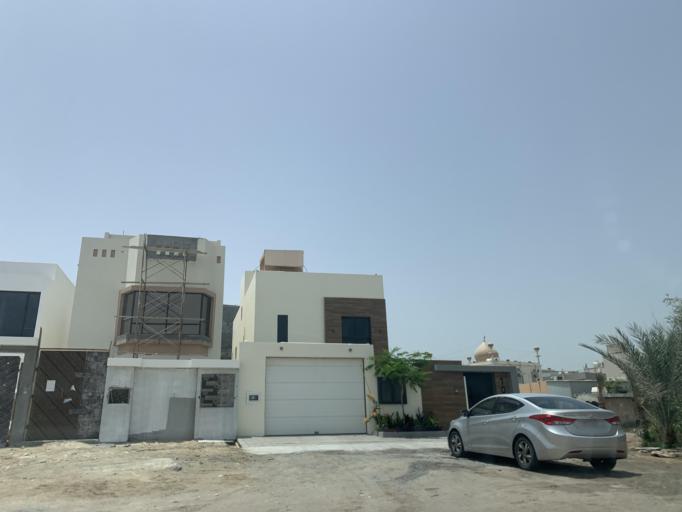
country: BH
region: Northern
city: Sitrah
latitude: 26.1497
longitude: 50.5878
